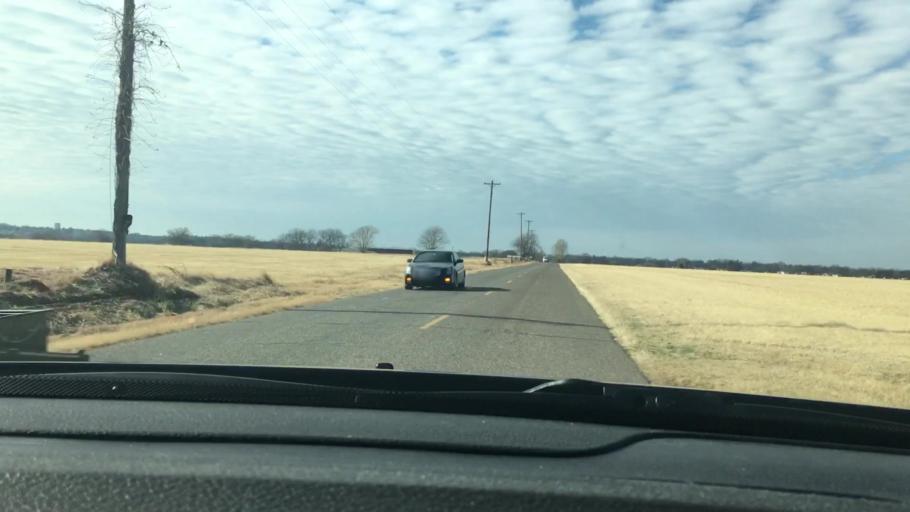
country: US
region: Oklahoma
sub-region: Garvin County
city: Pauls Valley
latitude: 34.7388
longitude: -97.1865
